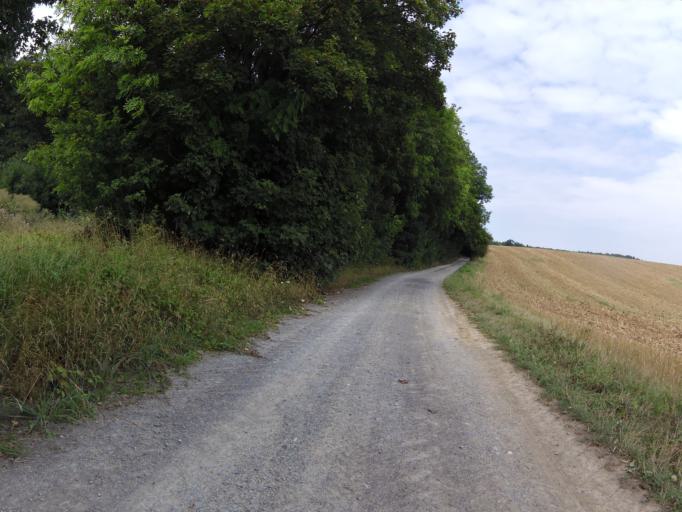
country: DE
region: Bavaria
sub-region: Regierungsbezirk Unterfranken
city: Kleinrinderfeld
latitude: 49.7036
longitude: 9.8295
